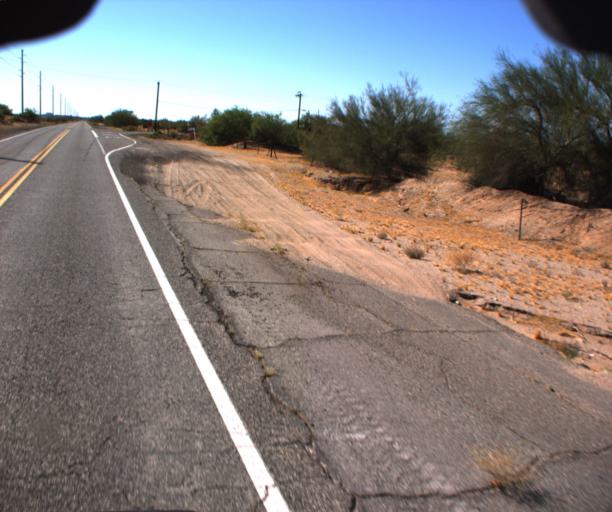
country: US
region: Arizona
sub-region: La Paz County
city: Cienega Springs
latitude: 33.9575
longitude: -114.0283
